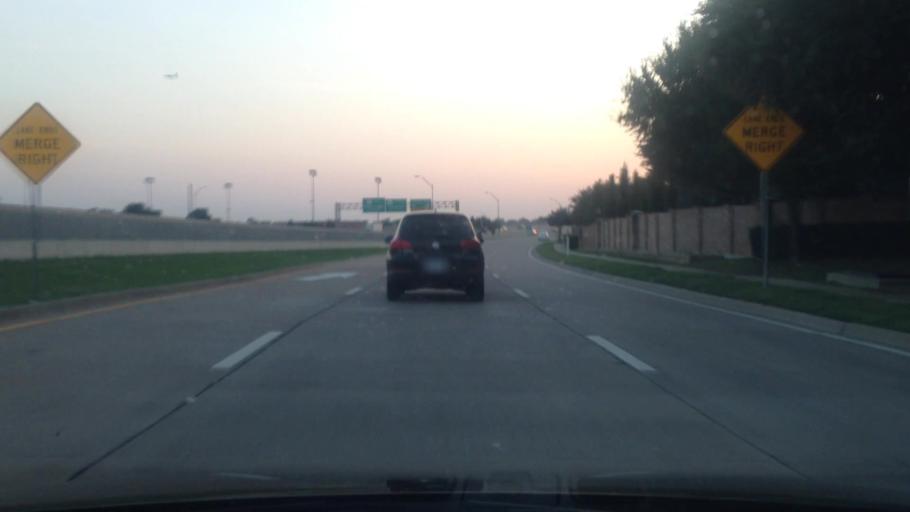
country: US
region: Texas
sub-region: Dallas County
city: Coppell
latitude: 32.9870
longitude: -96.9856
